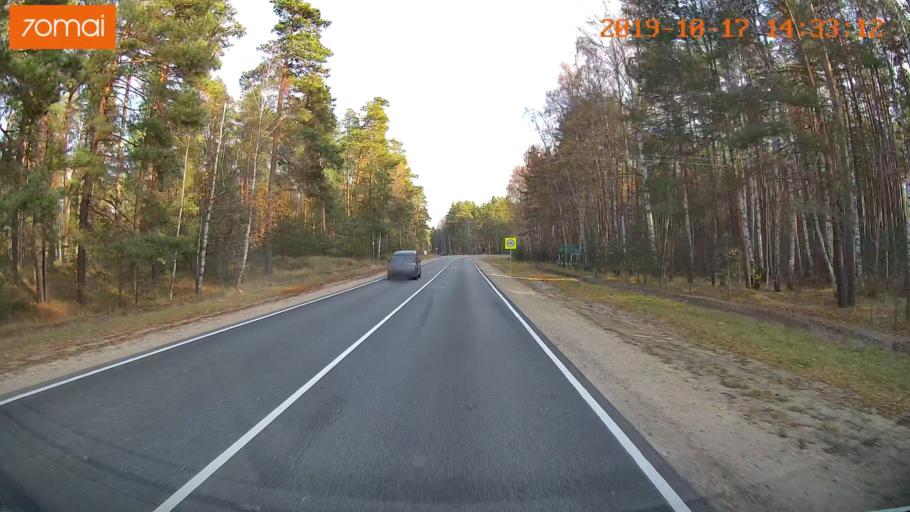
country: RU
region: Rjazan
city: Solotcha
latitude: 54.9246
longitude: 39.9940
